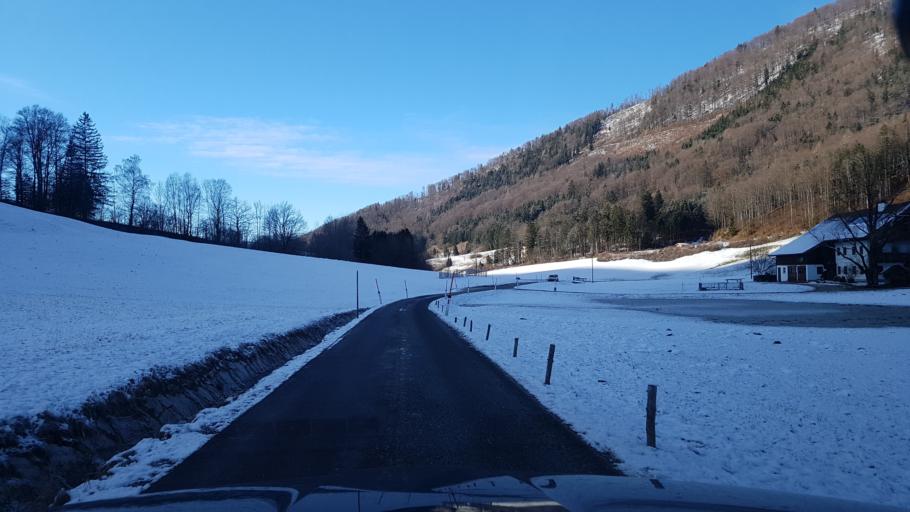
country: AT
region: Salzburg
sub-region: Politischer Bezirk Salzburg-Umgebung
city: Ebenau
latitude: 47.7783
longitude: 13.1513
